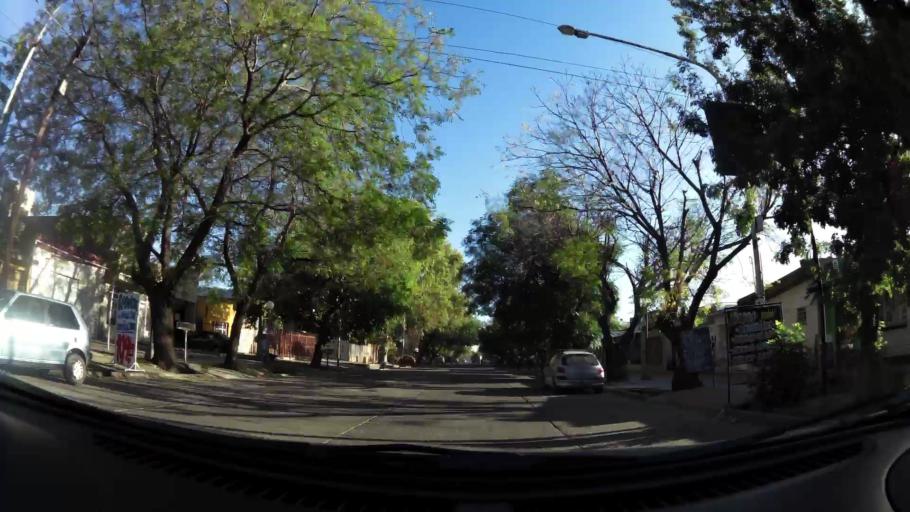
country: AR
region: Mendoza
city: Las Heras
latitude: -32.8653
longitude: -68.8223
